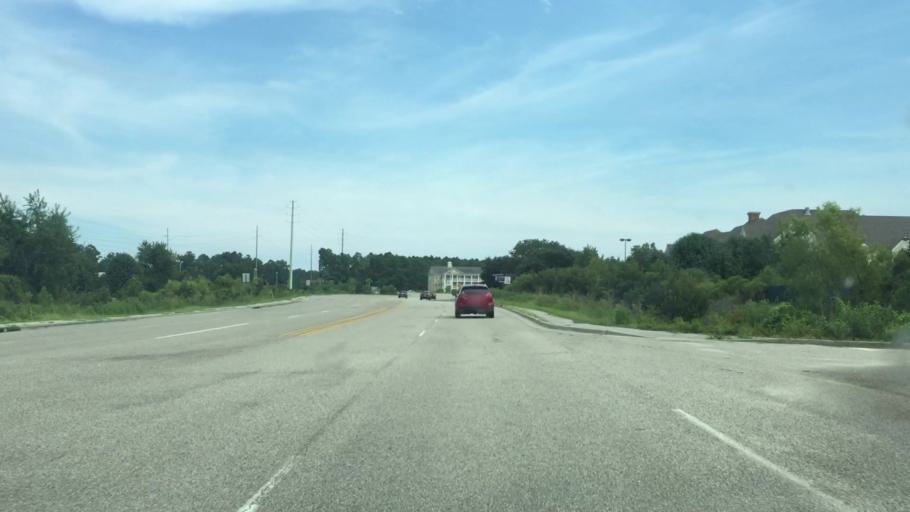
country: US
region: South Carolina
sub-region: Horry County
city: Forestbrook
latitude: 33.7153
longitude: -78.9297
